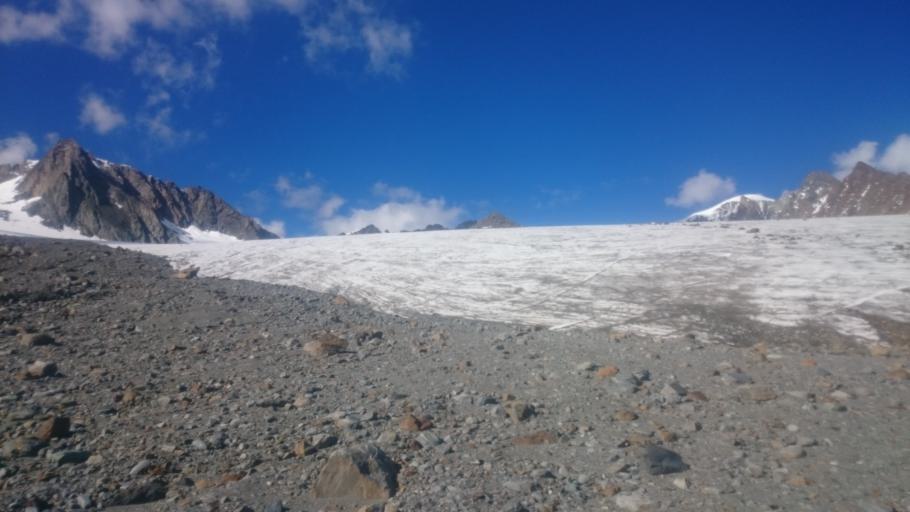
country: IT
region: Trentino-Alto Adige
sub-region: Bolzano
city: Senales
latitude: 46.8723
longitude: 10.8210
